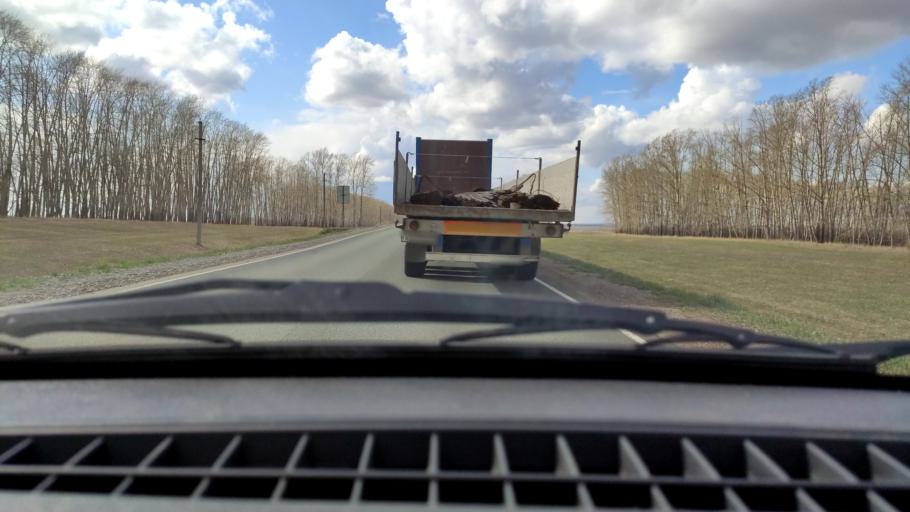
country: RU
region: Bashkortostan
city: Alekseyevka
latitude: 55.0571
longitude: 55.1151
